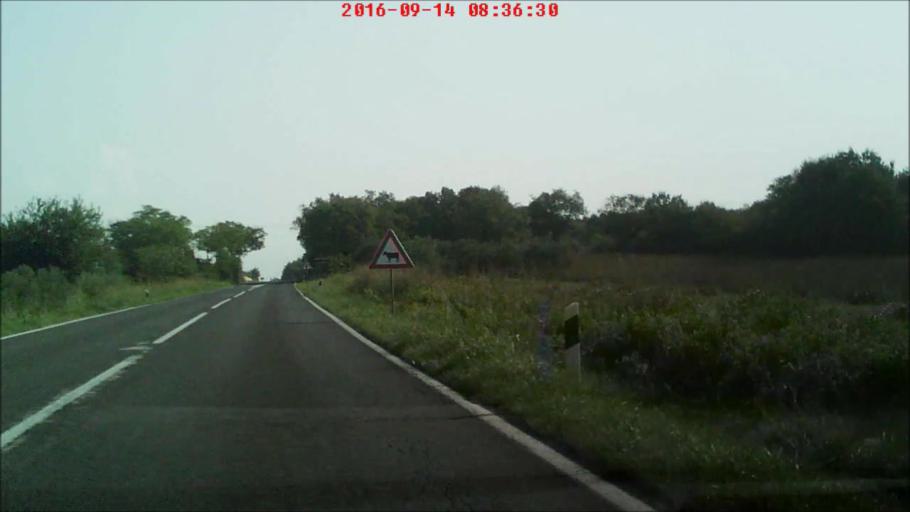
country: HR
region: Zadarska
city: Policnik
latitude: 44.1582
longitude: 15.3417
